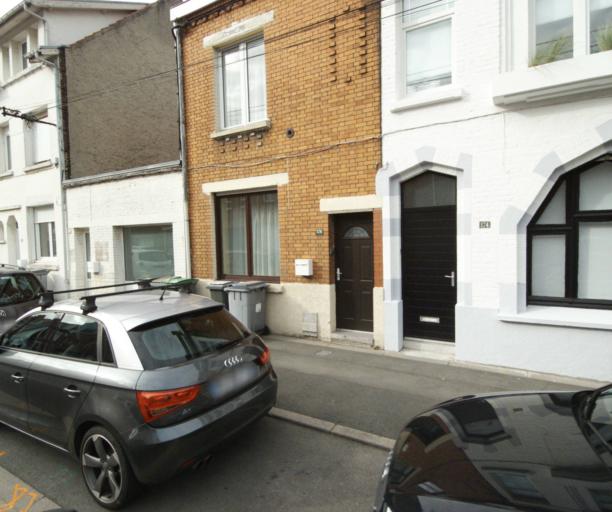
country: FR
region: Nord-Pas-de-Calais
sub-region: Departement du Nord
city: Lambersart
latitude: 50.6530
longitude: 3.0152
